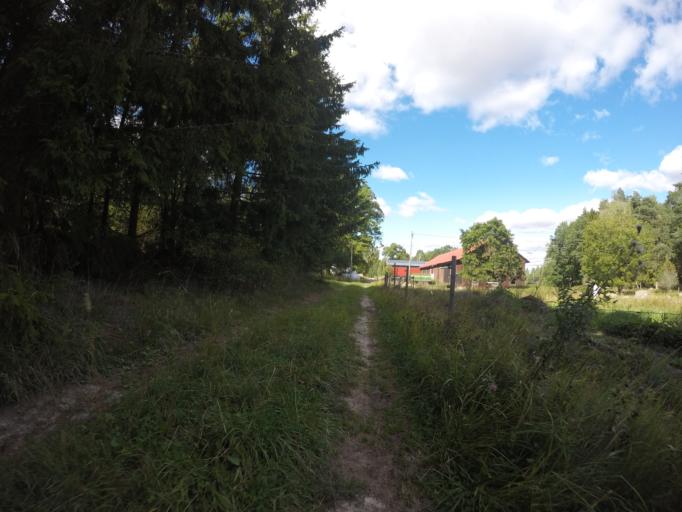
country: SE
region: Vaestmanland
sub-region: Hallstahammars Kommun
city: Kolback
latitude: 59.4949
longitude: 16.1984
